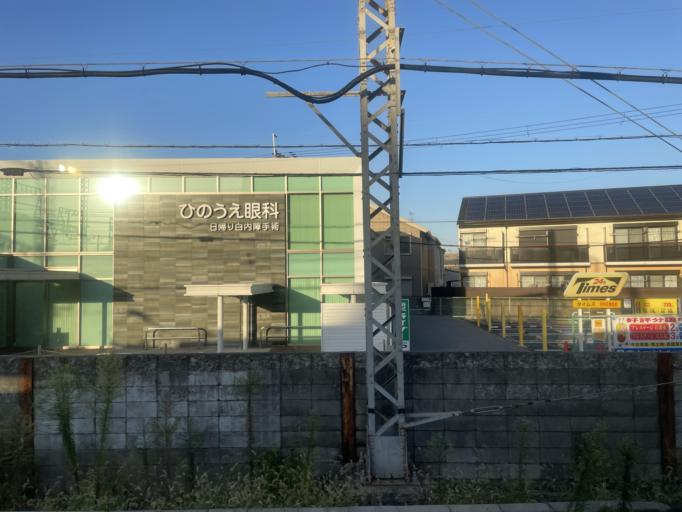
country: JP
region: Osaka
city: Matsubara
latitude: 34.5877
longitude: 135.5347
